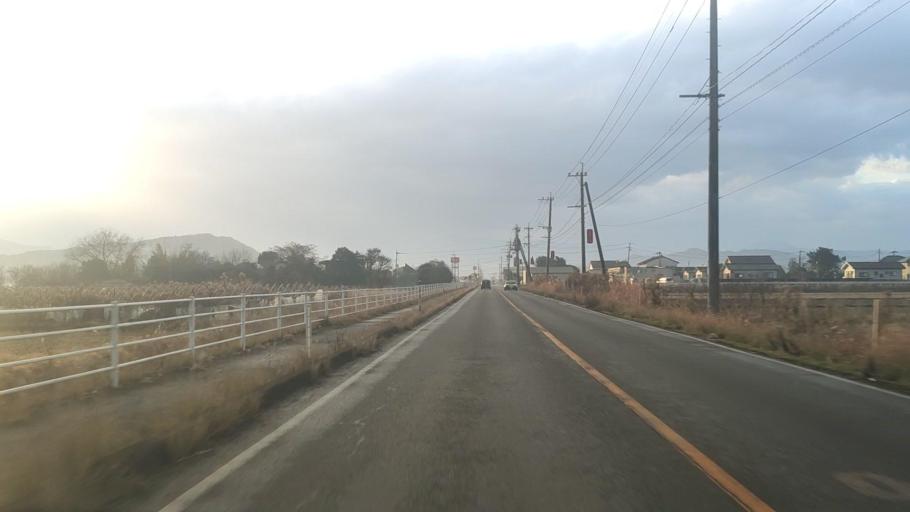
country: JP
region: Kumamoto
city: Uto
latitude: 32.7180
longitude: 130.7717
